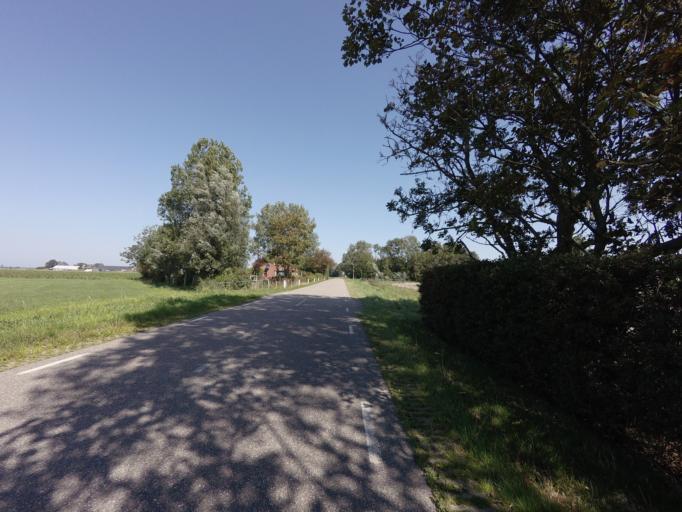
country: NL
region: Friesland
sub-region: Gemeente Dongeradeel
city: Ternaard
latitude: 53.3758
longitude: 6.0001
